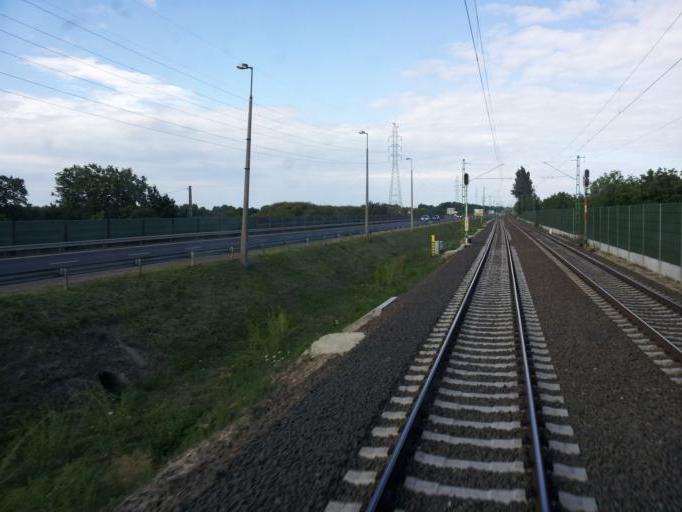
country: HU
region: Pest
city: Halasztelek
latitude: 47.3958
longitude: 19.0022
